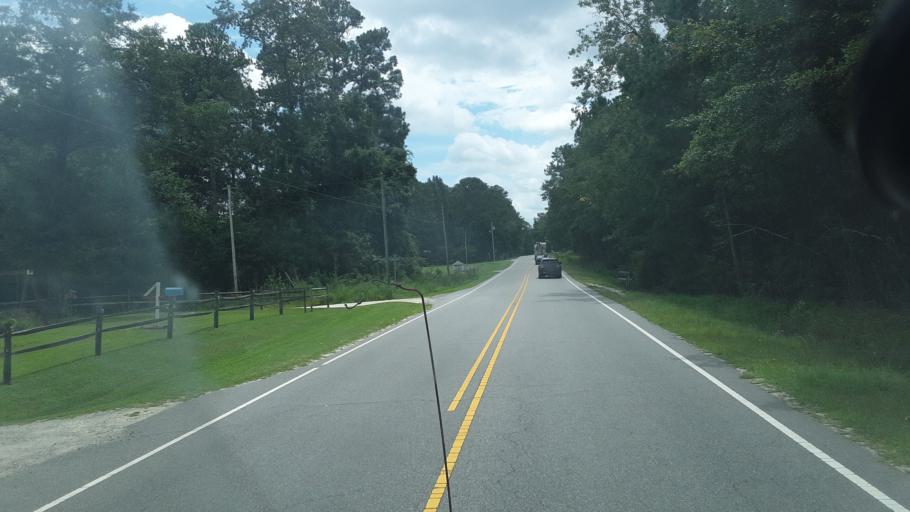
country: US
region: North Carolina
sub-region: Robeson County
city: Rowland
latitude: 34.4791
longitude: -79.2392
